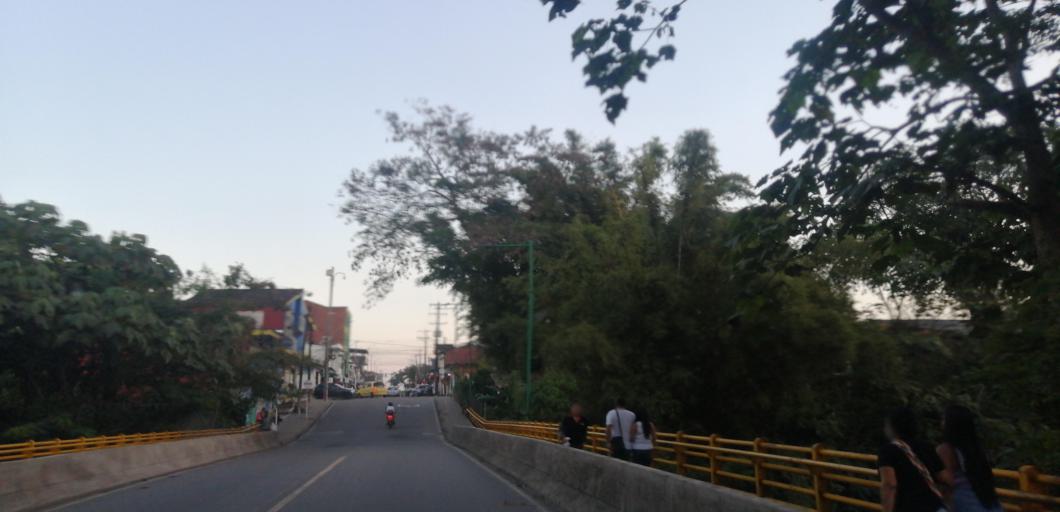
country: CO
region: Meta
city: Acacias
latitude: 3.9894
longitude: -73.7602
